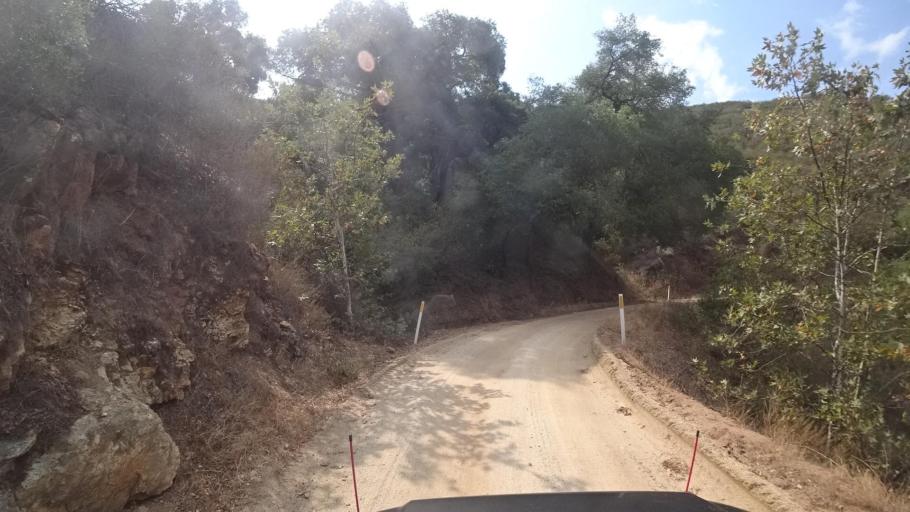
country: US
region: California
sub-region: San Diego County
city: Ramona
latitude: 33.1192
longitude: -116.8071
